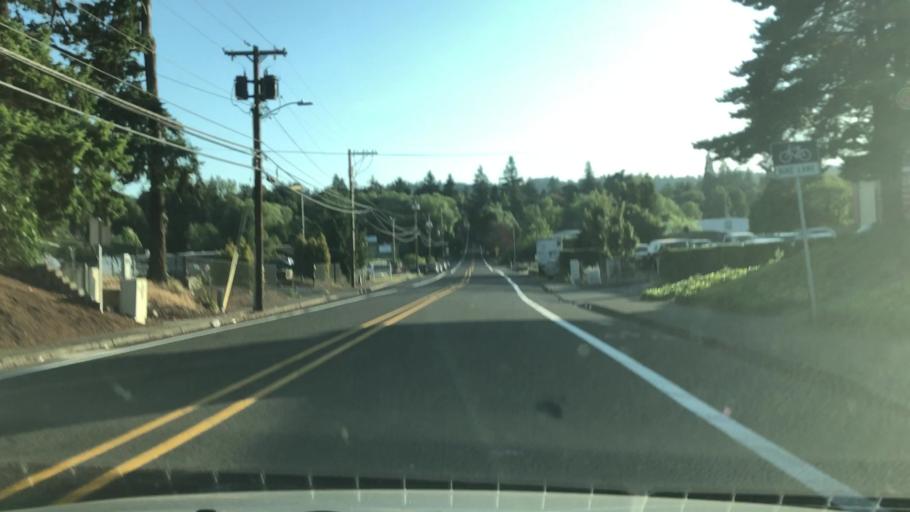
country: US
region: Oregon
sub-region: Clackamas County
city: Jennings Lodge
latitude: 45.3986
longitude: -122.6191
